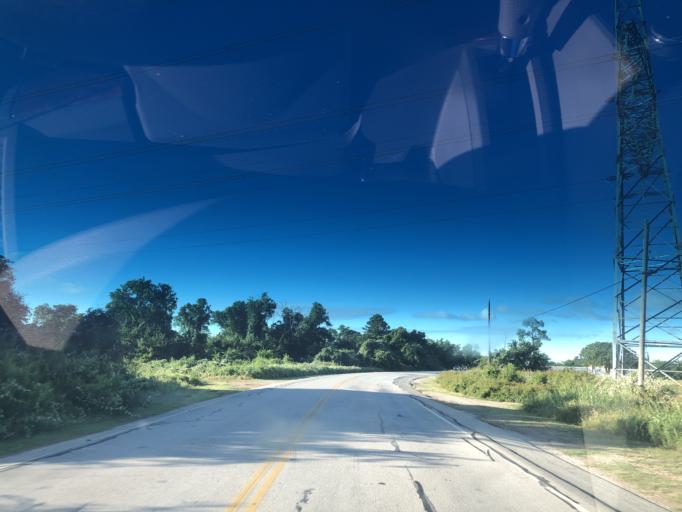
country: US
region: Texas
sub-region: Dallas County
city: Grand Prairie
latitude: 32.7853
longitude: -97.0170
